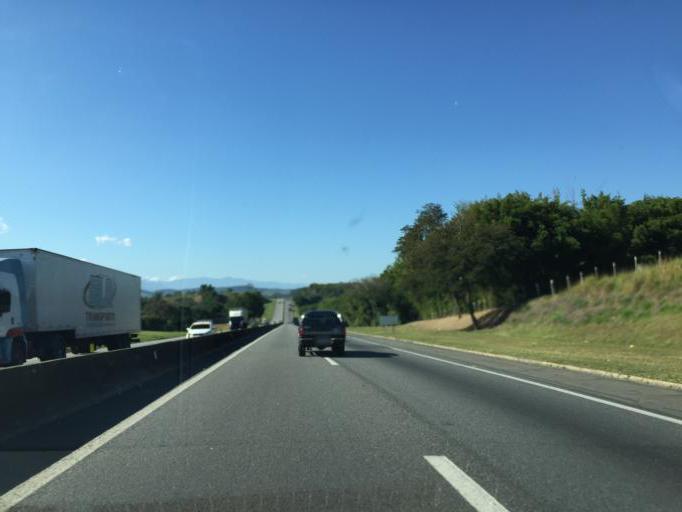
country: BR
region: Sao Paulo
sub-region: Lorena
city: Lorena
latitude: -22.6879
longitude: -45.0169
